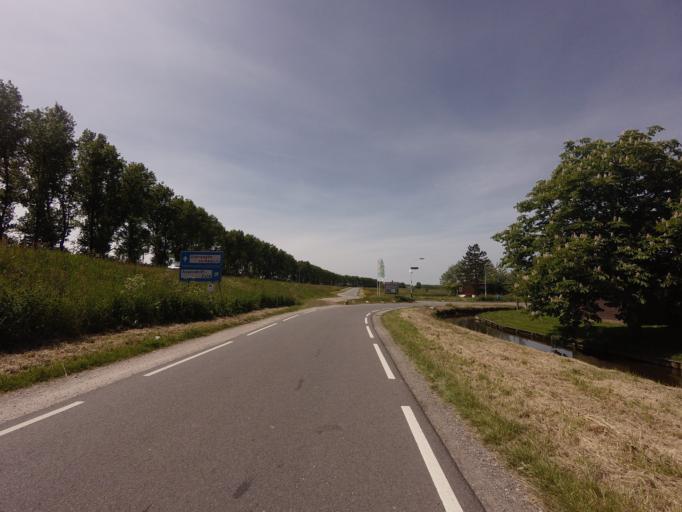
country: NL
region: North Holland
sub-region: Gemeente Velsen
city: Velsen-Zuid
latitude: 52.4376
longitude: 4.7163
